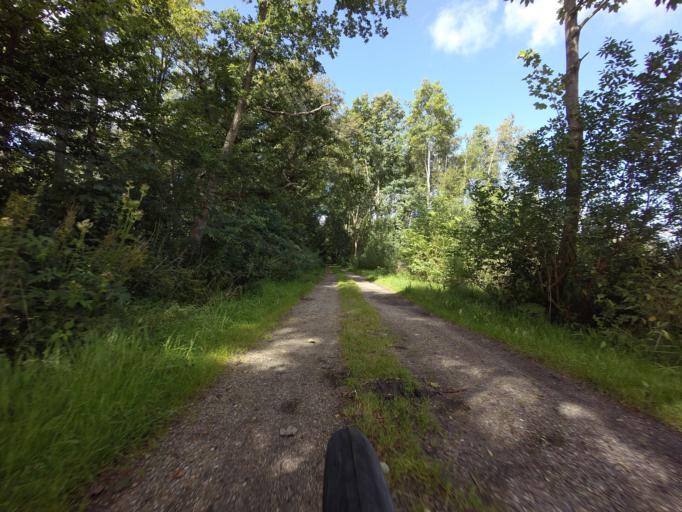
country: DK
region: Central Jutland
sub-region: Norddjurs Kommune
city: Auning
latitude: 56.4383
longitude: 10.3577
